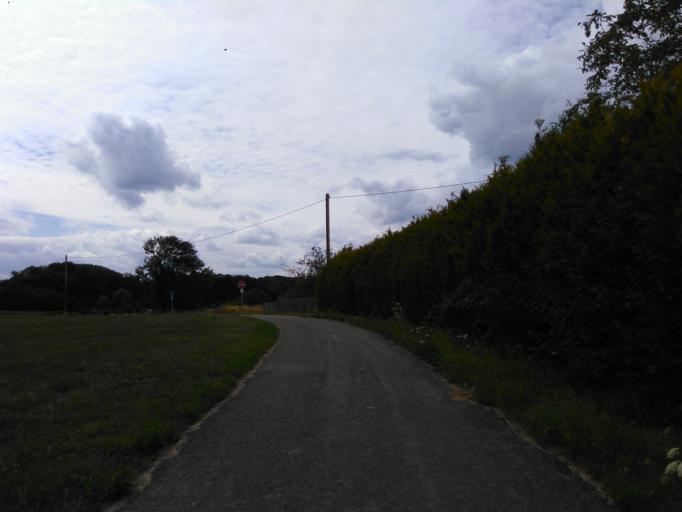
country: LU
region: Grevenmacher
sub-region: Canton d'Echternach
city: Consdorf
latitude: 49.7631
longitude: 6.3512
